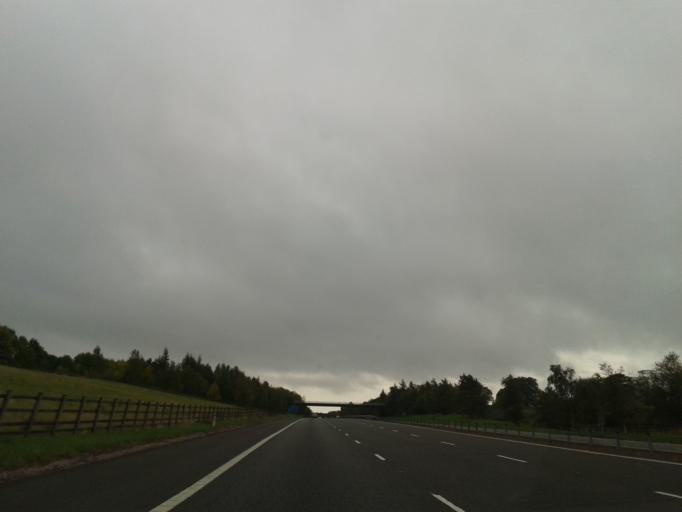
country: GB
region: Scotland
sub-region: Dumfries and Galloway
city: Lockerbie
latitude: 55.1271
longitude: -3.3656
